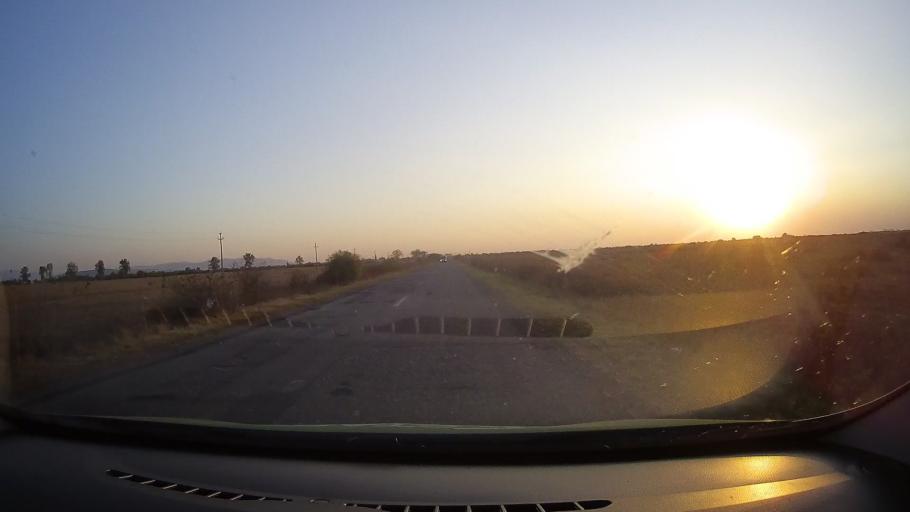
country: RO
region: Arad
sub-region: Comuna Seleus
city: Seleus
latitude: 46.3963
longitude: 21.7185
